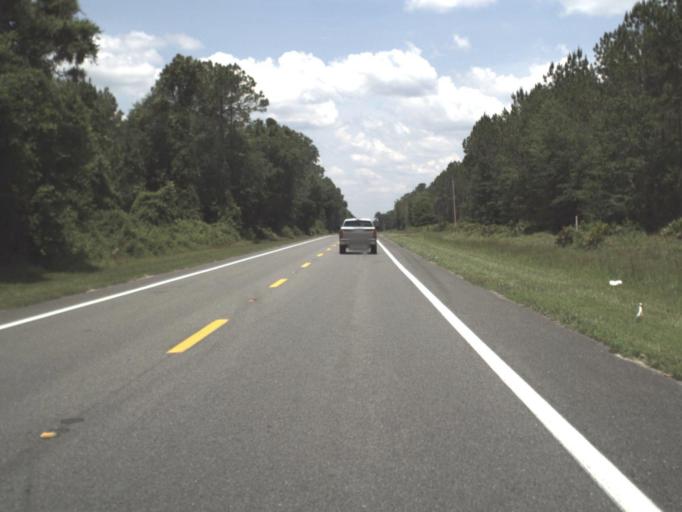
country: US
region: Florida
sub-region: Union County
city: Lake Butler
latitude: 30.0654
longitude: -82.4305
